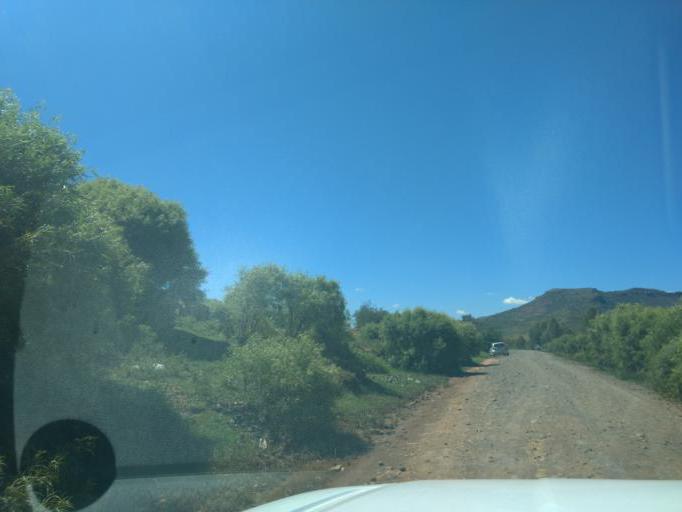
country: LS
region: Maseru
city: Maseru
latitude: -29.4887
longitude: 27.3711
